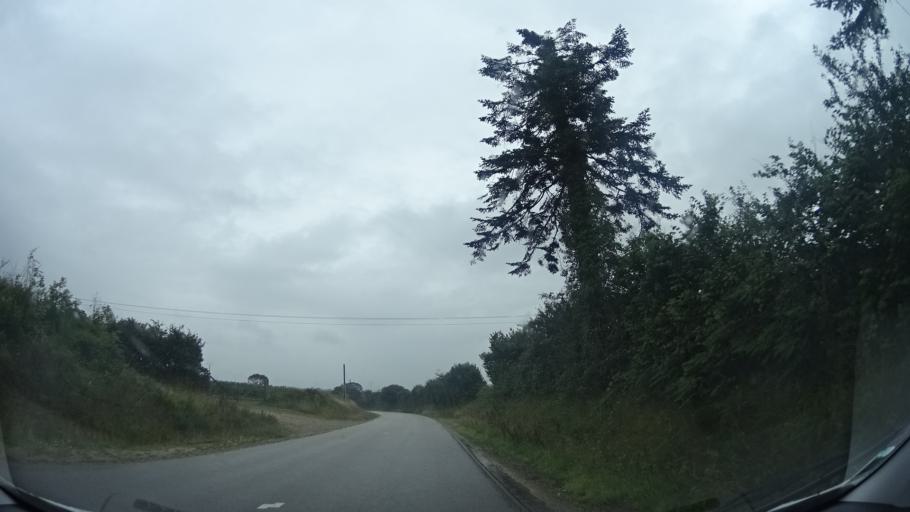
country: FR
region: Lower Normandy
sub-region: Departement de la Manche
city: Urville-Nacqueville
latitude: 49.5955
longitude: -1.7626
